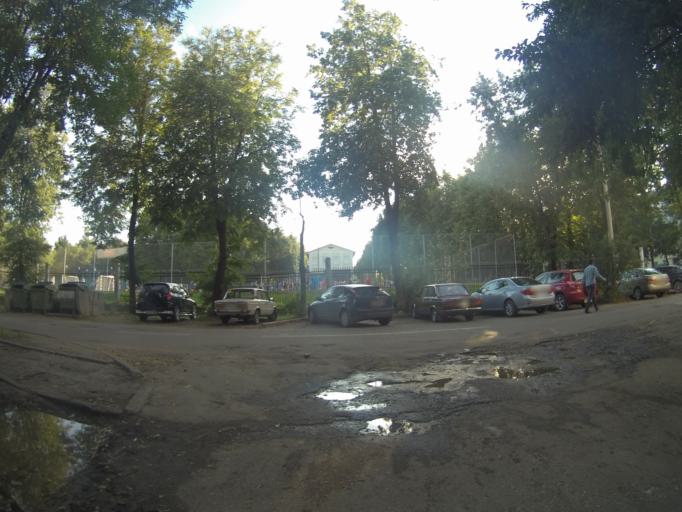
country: RU
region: Vladimir
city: Vladimir
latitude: 56.1439
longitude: 40.4163
